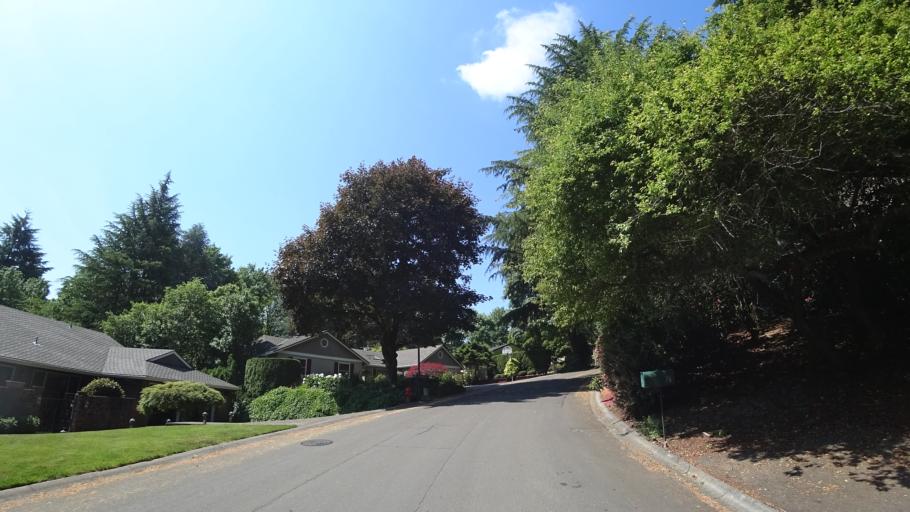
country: US
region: Oregon
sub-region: Clackamas County
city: Lake Oswego
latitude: 45.4279
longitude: -122.7094
